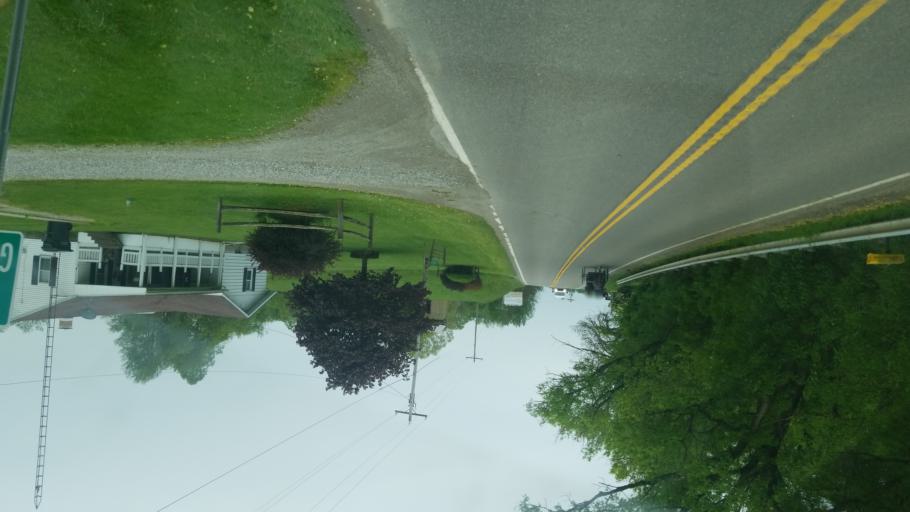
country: US
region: Ohio
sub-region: Tuscarawas County
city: Newcomerstown
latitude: 40.2188
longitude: -81.5114
